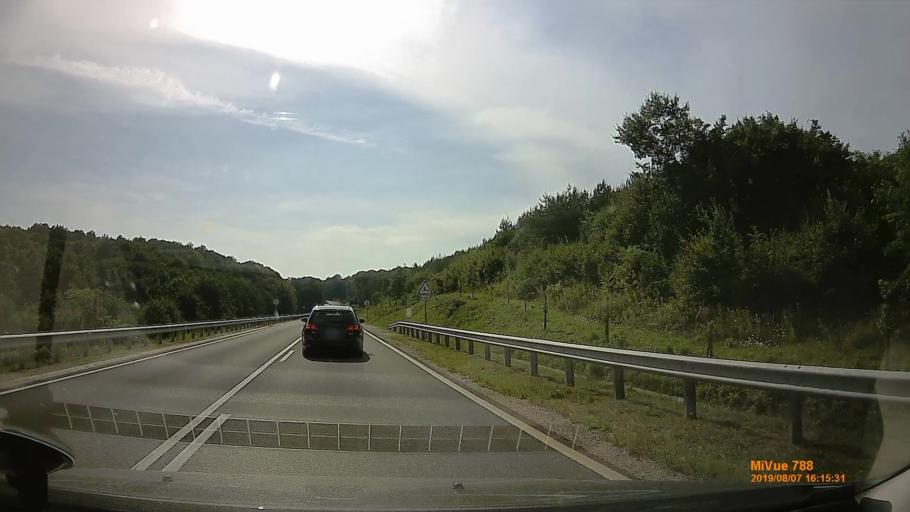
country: HU
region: Zala
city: Zalalovo
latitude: 46.8251
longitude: 16.5960
